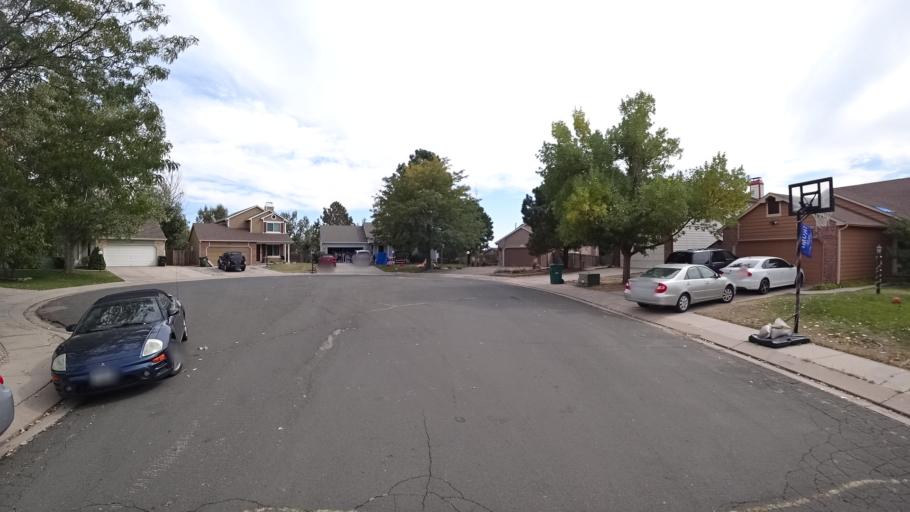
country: US
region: Colorado
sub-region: El Paso County
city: Cimarron Hills
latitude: 38.9021
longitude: -104.7016
